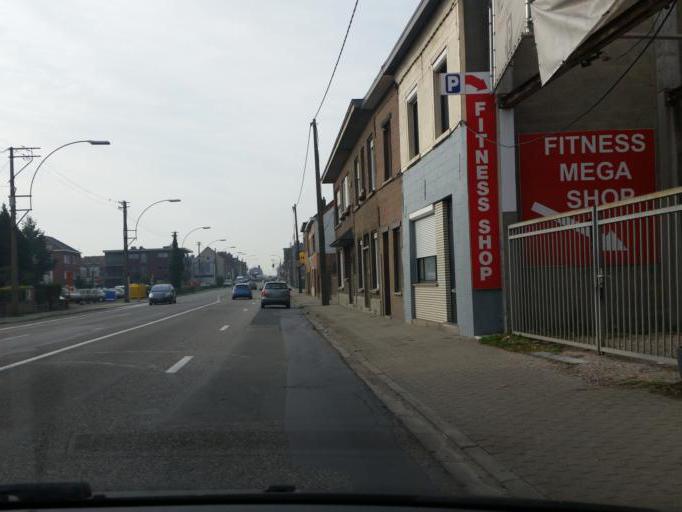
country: BE
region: Flanders
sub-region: Provincie Vlaams-Brabant
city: Drogenbos
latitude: 50.7950
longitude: 4.2844
